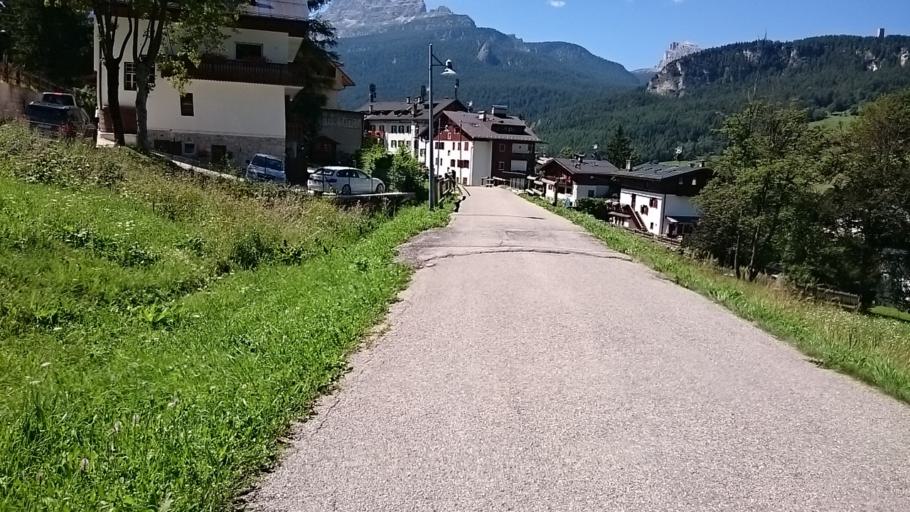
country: IT
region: Veneto
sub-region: Provincia di Belluno
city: Cortina d'Ampezzo
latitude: 46.5337
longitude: 12.1426
